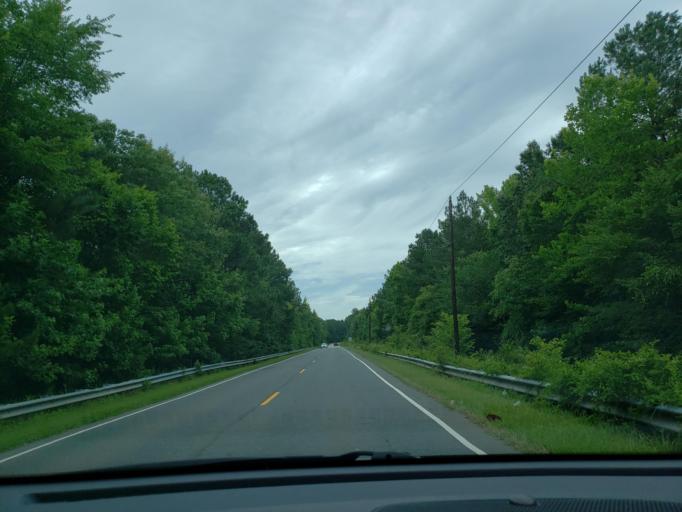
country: US
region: North Carolina
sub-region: Orange County
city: Chapel Hill
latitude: 35.8618
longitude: -79.0092
